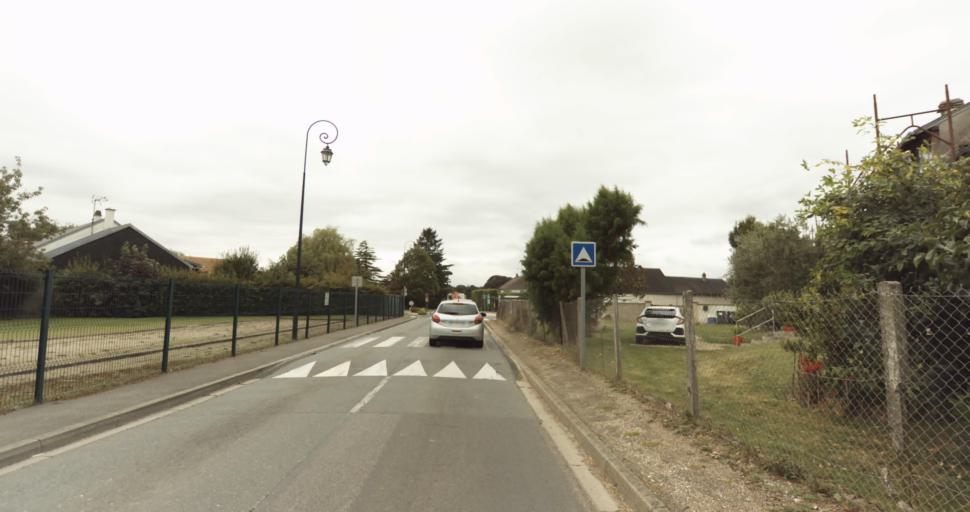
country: FR
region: Haute-Normandie
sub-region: Departement de l'Eure
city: Gravigny
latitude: 49.0317
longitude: 1.1972
